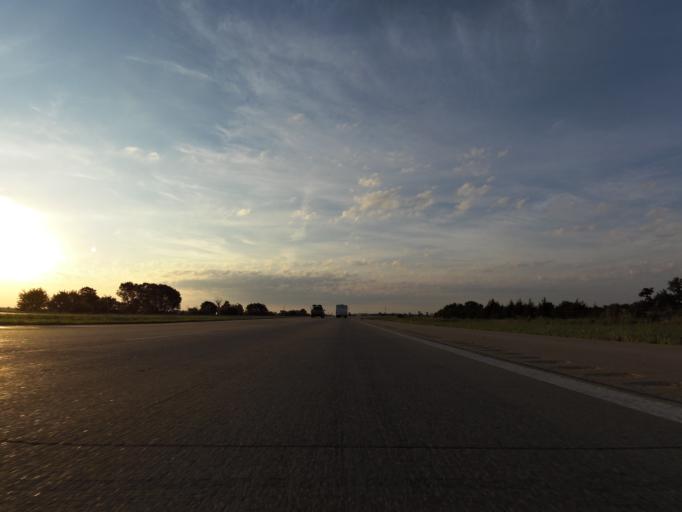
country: US
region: Kansas
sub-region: Reno County
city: South Hutchinson
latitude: 37.9494
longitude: -97.8907
